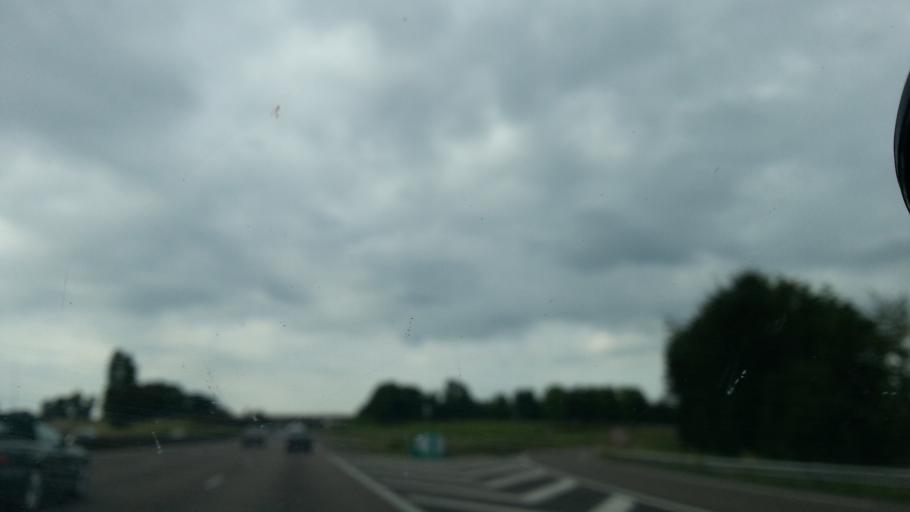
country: FR
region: Bourgogne
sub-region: Departement de Saone-et-Loire
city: Champforgeuil
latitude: 46.8072
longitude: 4.8260
